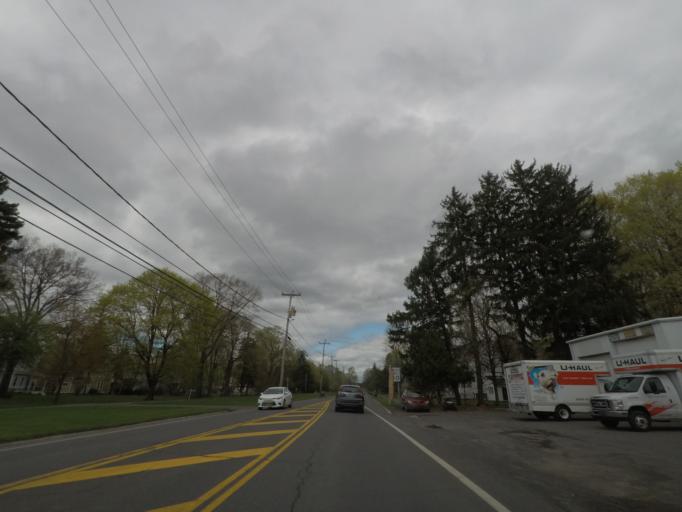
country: US
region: New York
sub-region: Columbia County
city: Chatham
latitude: 42.3509
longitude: -73.6034
